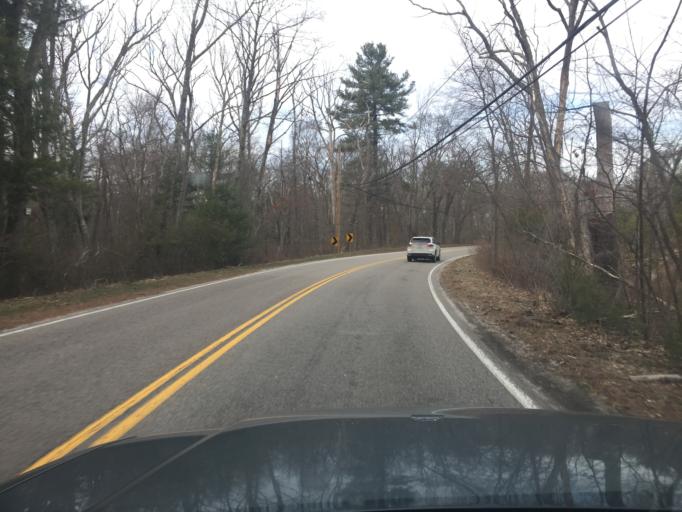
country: US
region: Massachusetts
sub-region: Middlesex County
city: Sherborn
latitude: 42.2082
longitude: -71.3584
